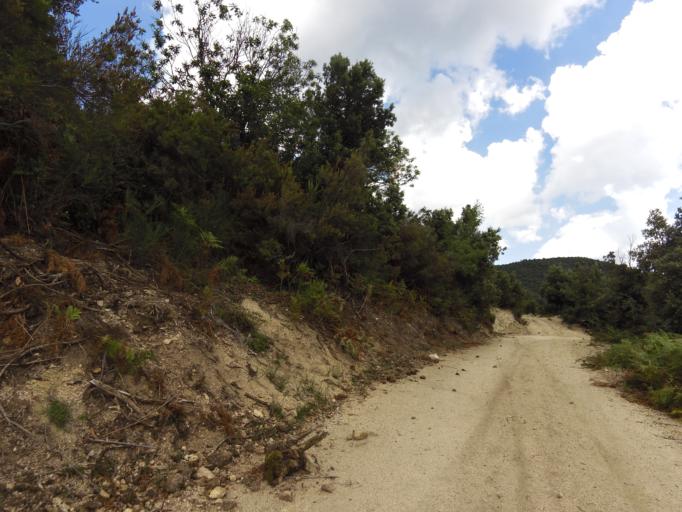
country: IT
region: Calabria
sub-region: Provincia di Reggio Calabria
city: Bivongi
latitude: 38.5085
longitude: 16.3965
